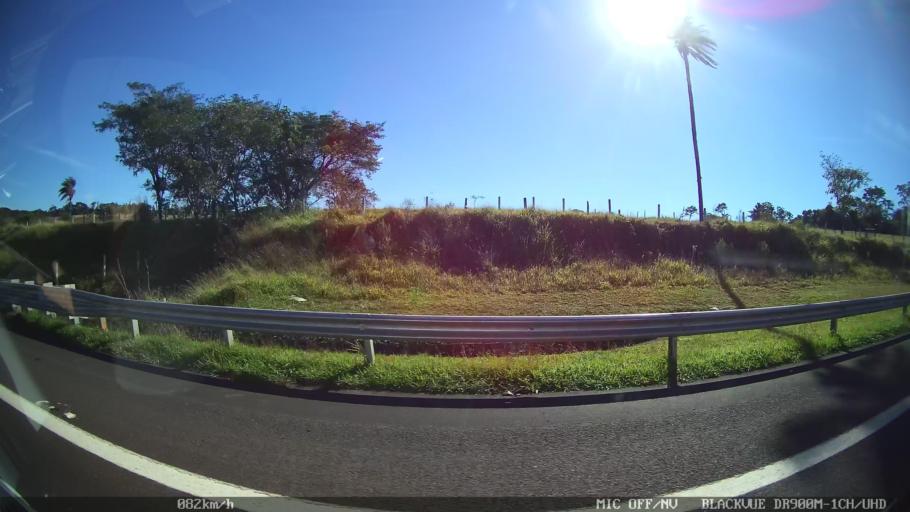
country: BR
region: Sao Paulo
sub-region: Franca
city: Franca
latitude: -20.5758
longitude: -47.3583
